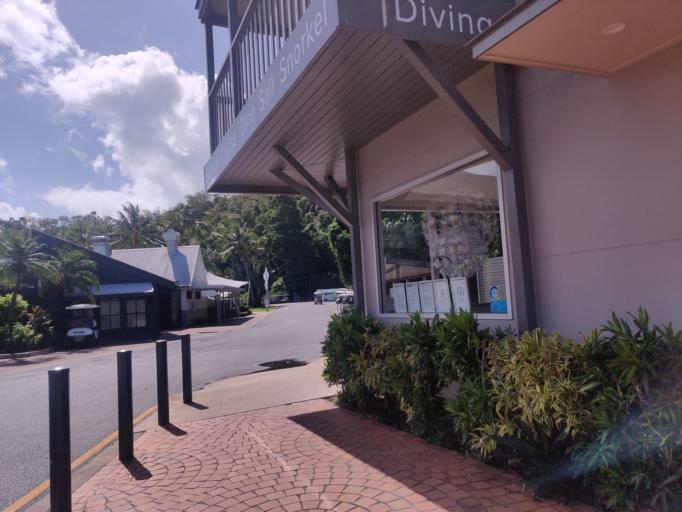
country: AU
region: Queensland
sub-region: Whitsunday
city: Proserpine
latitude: -20.3454
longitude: 148.9512
